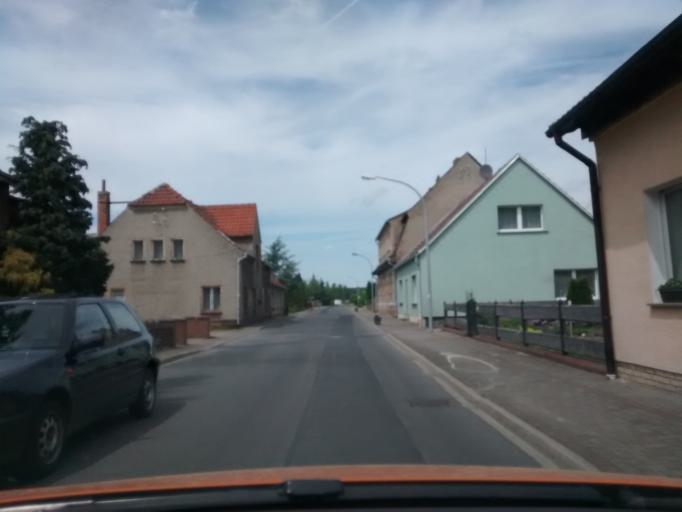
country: DE
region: Saxony-Anhalt
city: Holzdorf
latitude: 51.8152
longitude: 13.2324
